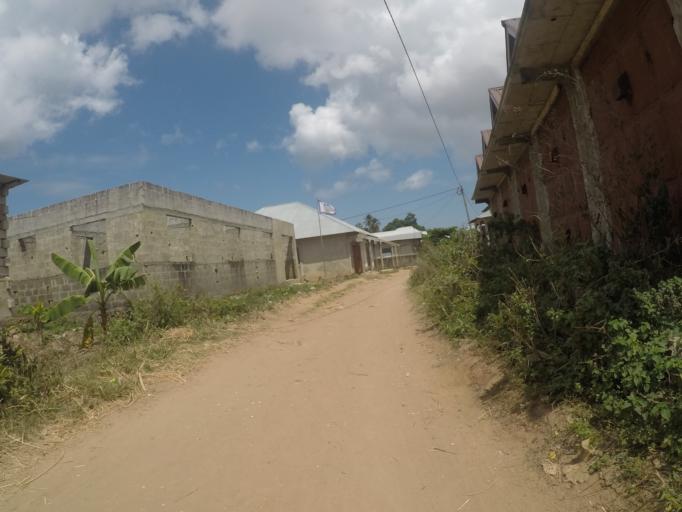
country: TZ
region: Zanzibar Urban/West
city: Zanzibar
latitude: -6.2015
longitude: 39.2368
